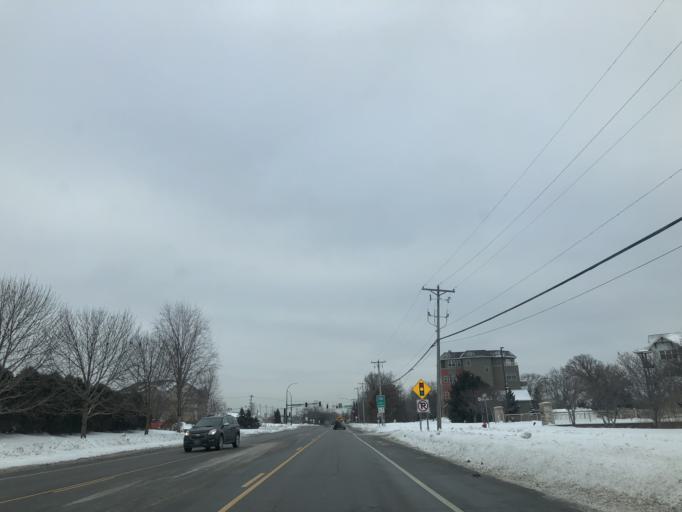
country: US
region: Minnesota
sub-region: Ramsey County
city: New Brighton
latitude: 45.0809
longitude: -93.1883
